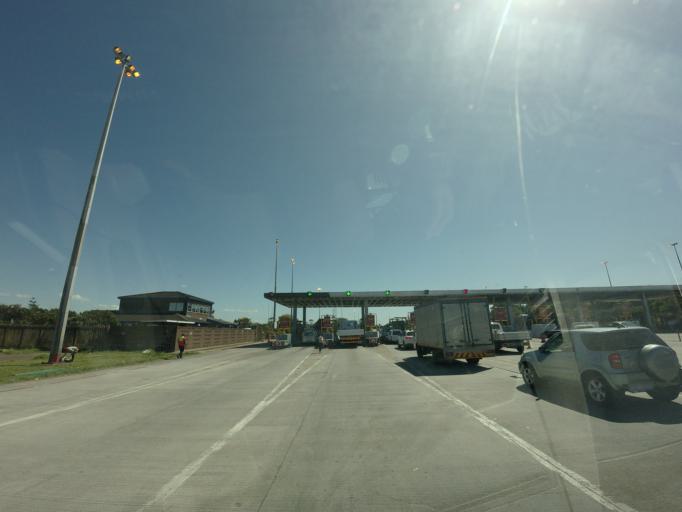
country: ZA
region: KwaZulu-Natal
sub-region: iLembe District Municipality
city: Stanger
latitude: -29.4040
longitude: 31.2848
